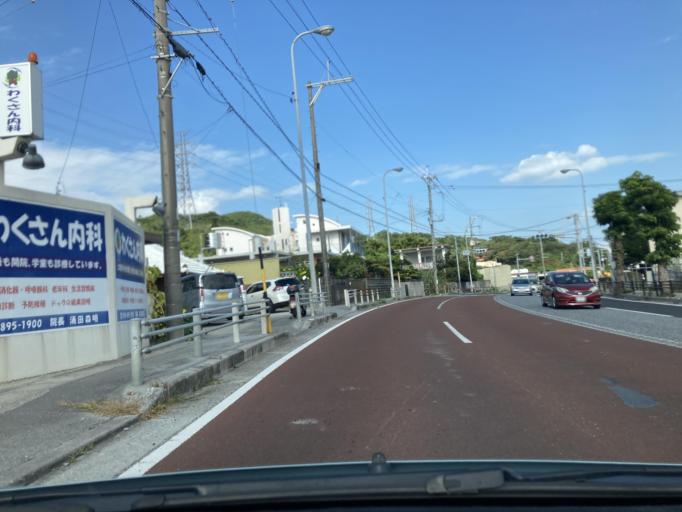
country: JP
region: Okinawa
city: Ginowan
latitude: 26.2709
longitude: 127.7918
